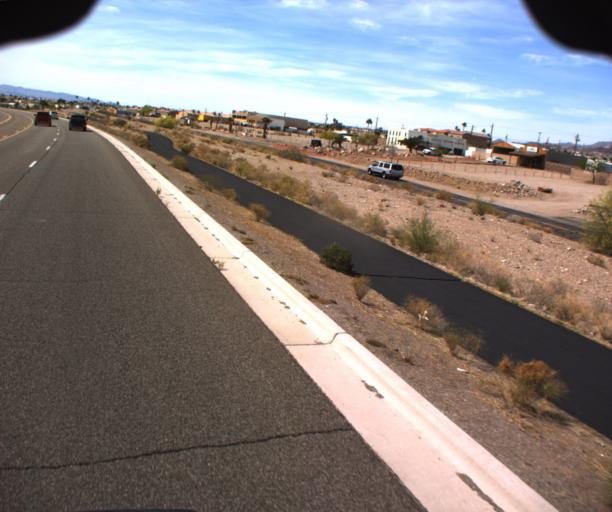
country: US
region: Arizona
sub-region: Mohave County
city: Lake Havasu City
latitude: 34.4544
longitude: -114.2677
